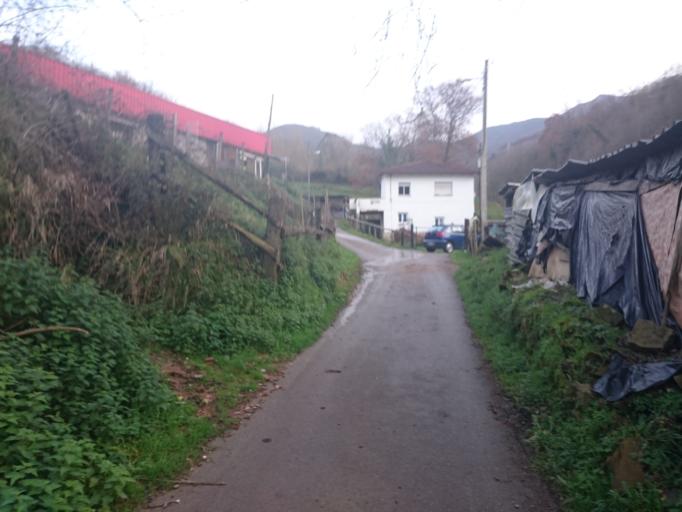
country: ES
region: Asturias
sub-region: Province of Asturias
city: Oviedo
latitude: 43.3180
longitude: -5.7988
